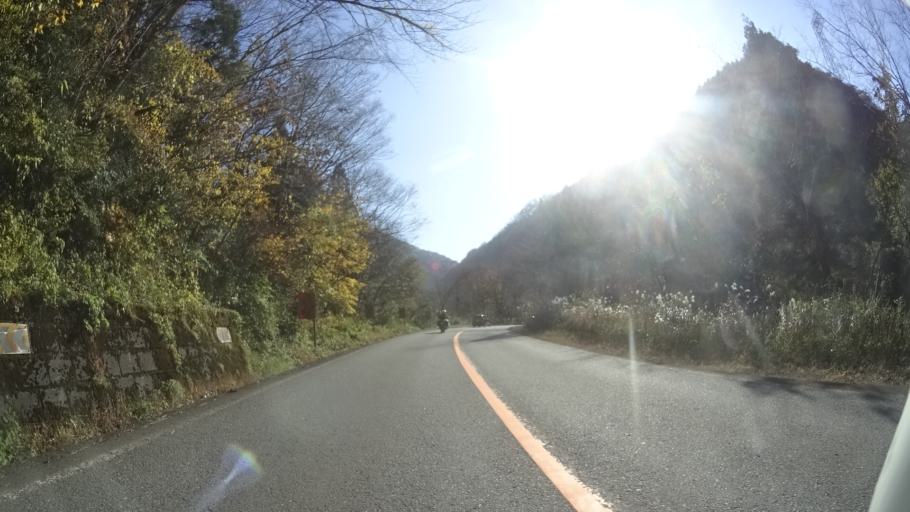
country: JP
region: Fukui
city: Ono
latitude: 35.9493
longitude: 136.6401
